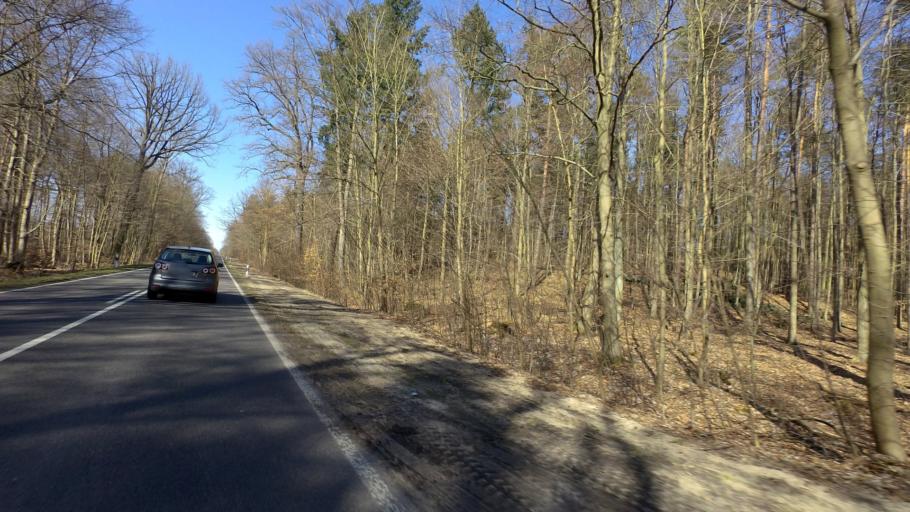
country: DE
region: Brandenburg
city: Eberswalde
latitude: 52.8107
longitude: 13.8341
